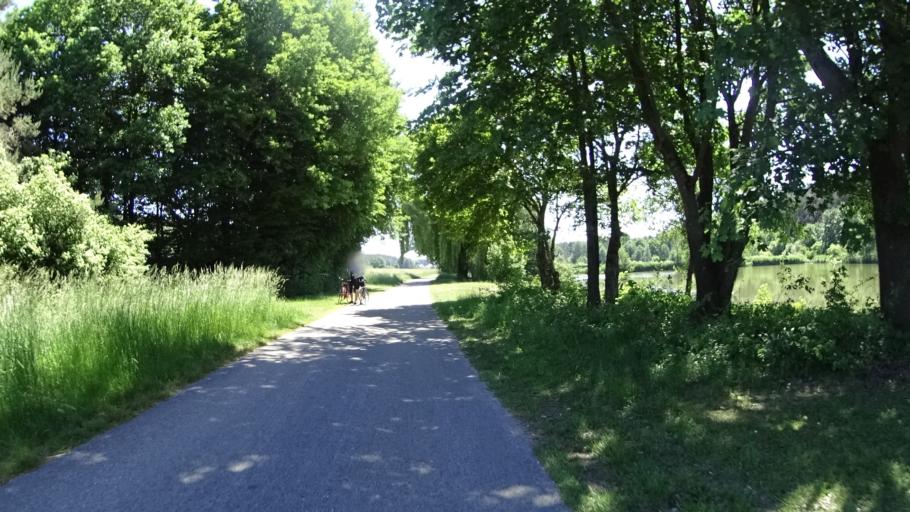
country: DE
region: Bavaria
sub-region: Regierungsbezirk Mittelfranken
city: Pleinfeld
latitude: 49.1095
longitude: 10.9381
